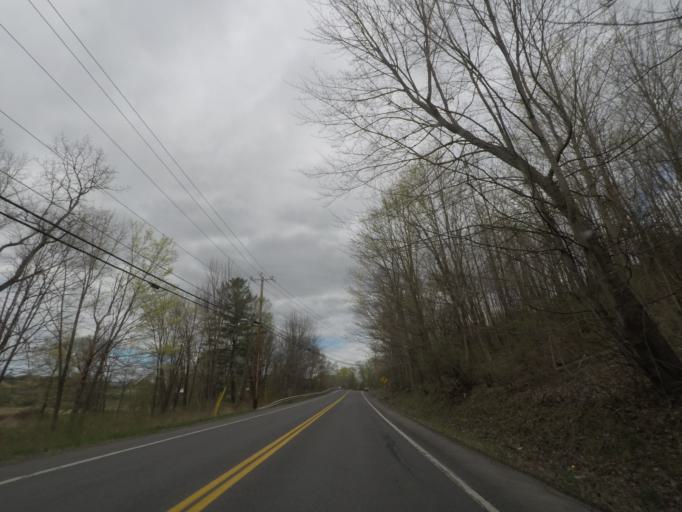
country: US
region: New York
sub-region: Columbia County
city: Chatham
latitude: 42.3414
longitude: -73.6093
